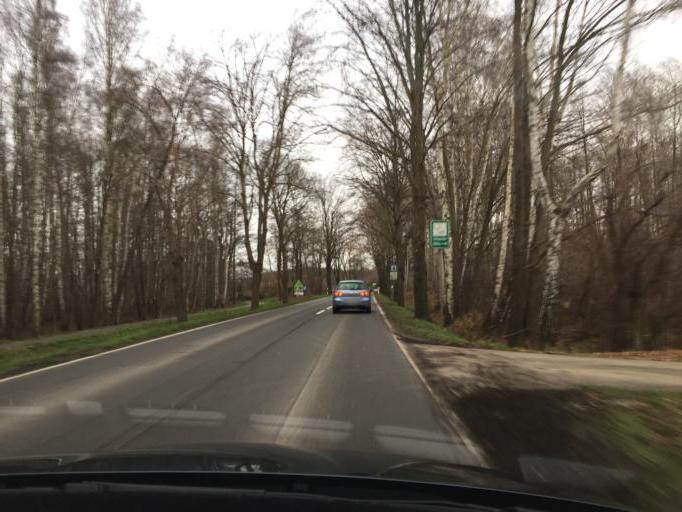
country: DE
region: Brandenburg
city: Burg
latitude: 51.8237
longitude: 14.1382
